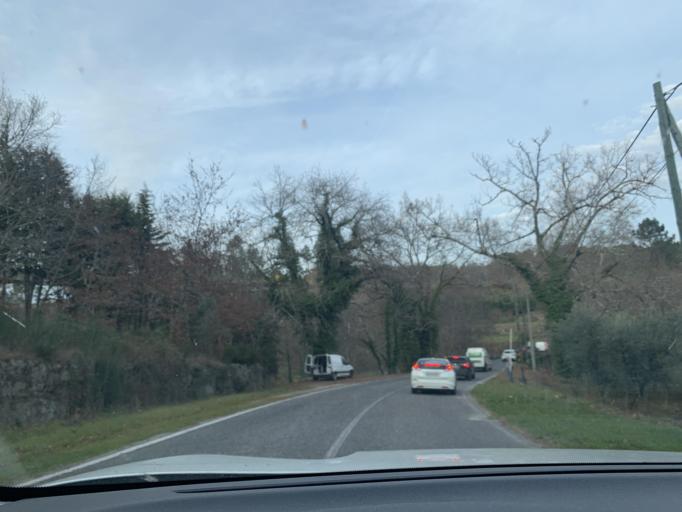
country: PT
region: Viseu
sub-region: Viseu
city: Viseu
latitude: 40.6005
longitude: -7.9937
